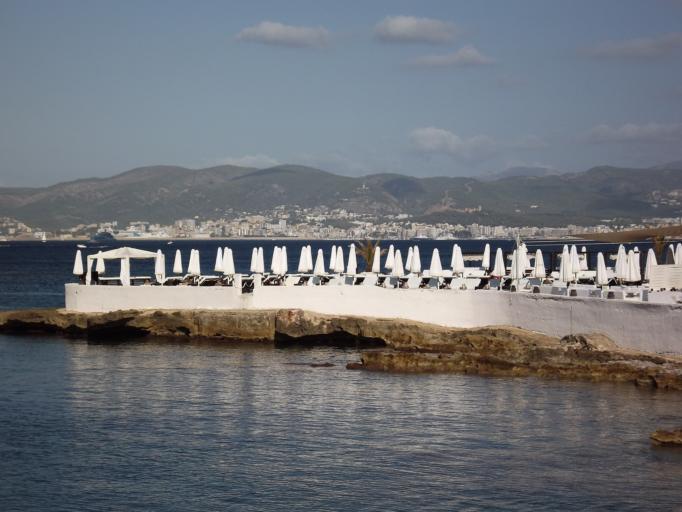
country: ES
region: Balearic Islands
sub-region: Illes Balears
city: s'Arenal
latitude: 39.5348
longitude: 2.7105
